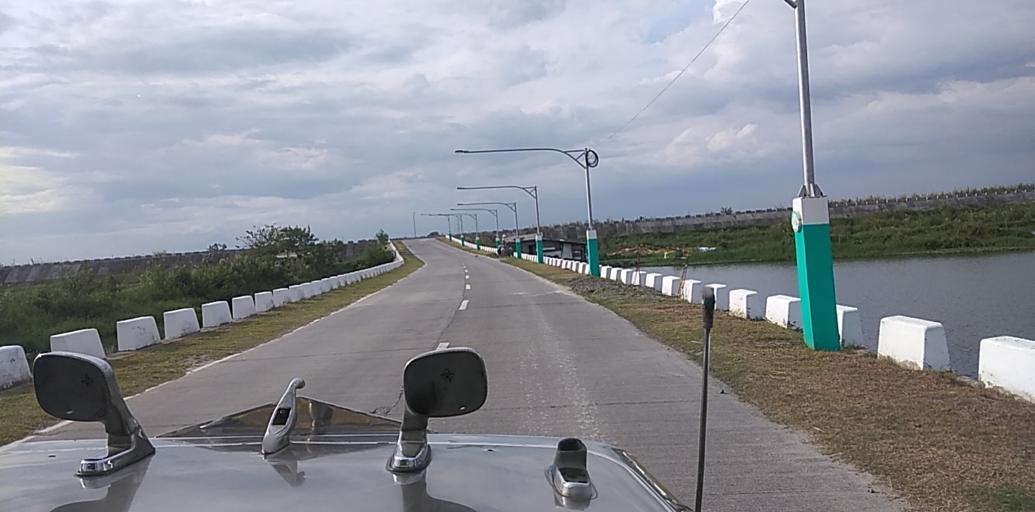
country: PH
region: Central Luzon
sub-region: Province of Pampanga
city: Minalin
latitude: 14.9752
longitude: 120.6822
